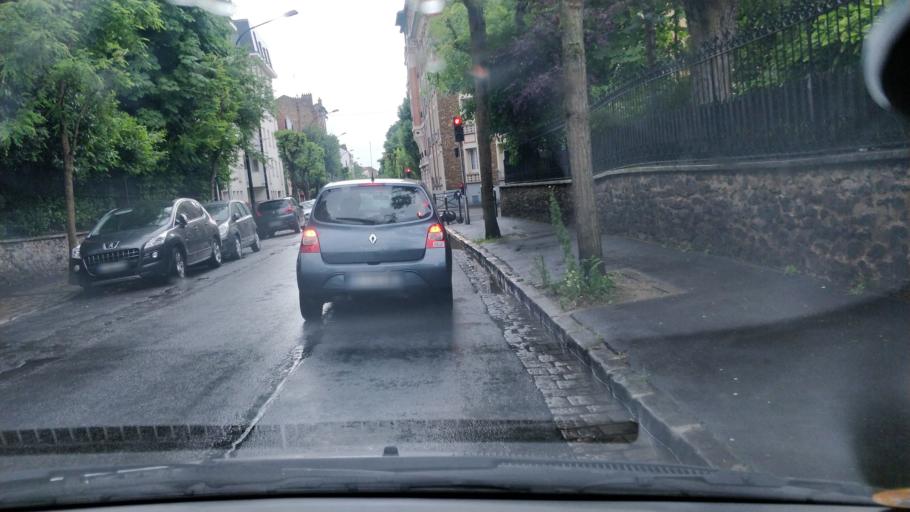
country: FR
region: Ile-de-France
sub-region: Departement de Seine-Saint-Denis
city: Le Raincy
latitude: 48.8931
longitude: 2.5095
